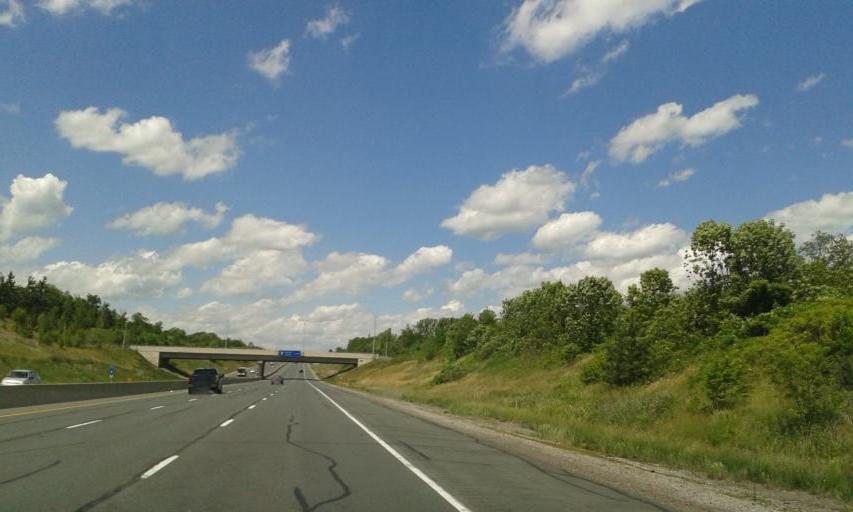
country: CA
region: Ontario
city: Burlington
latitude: 43.3564
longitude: -79.8315
